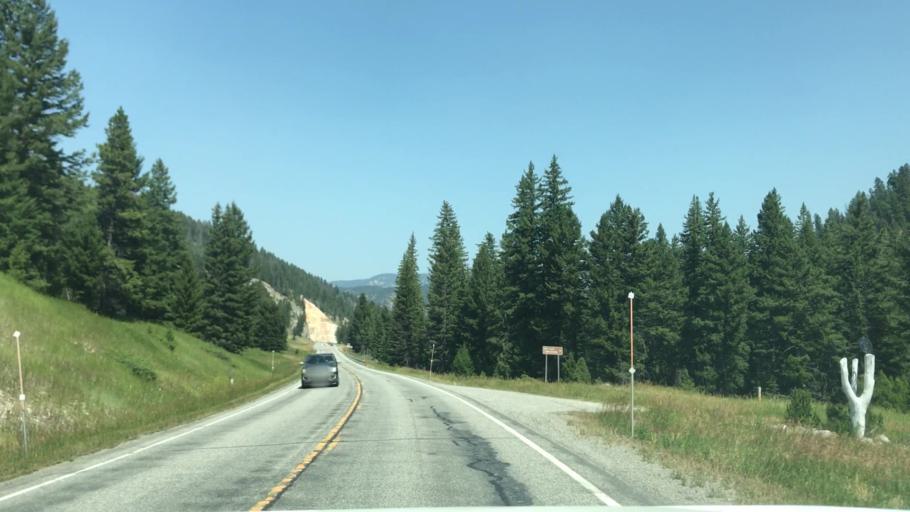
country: US
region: Montana
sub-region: Gallatin County
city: Big Sky
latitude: 45.1694
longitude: -111.2439
